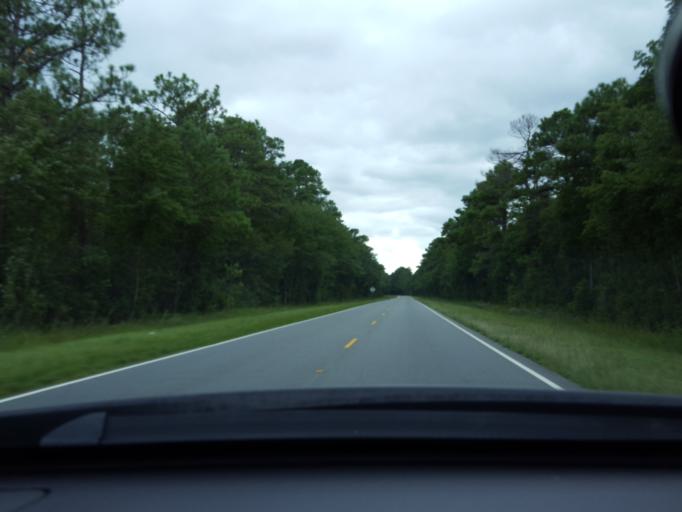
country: US
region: North Carolina
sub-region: Bladen County
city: Elizabethtown
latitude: 34.7065
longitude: -78.4670
